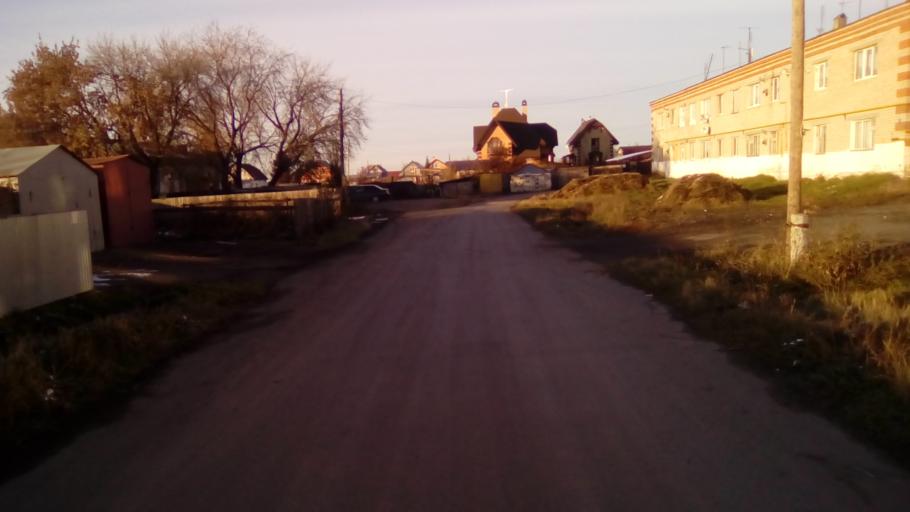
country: RU
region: Tjumen
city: Moskovskiy
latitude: 57.2210
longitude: 65.3552
